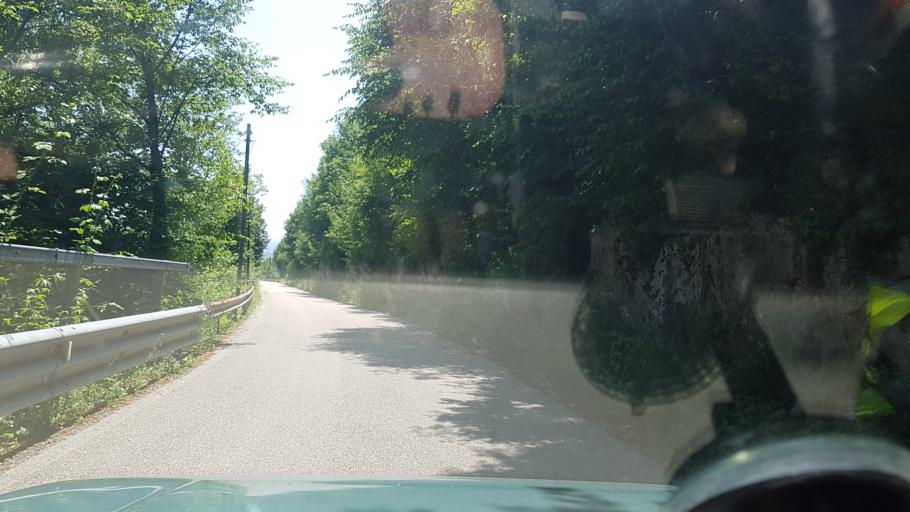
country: IT
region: Friuli Venezia Giulia
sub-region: Provincia di Udine
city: Nimis
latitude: 46.2319
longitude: 13.2776
